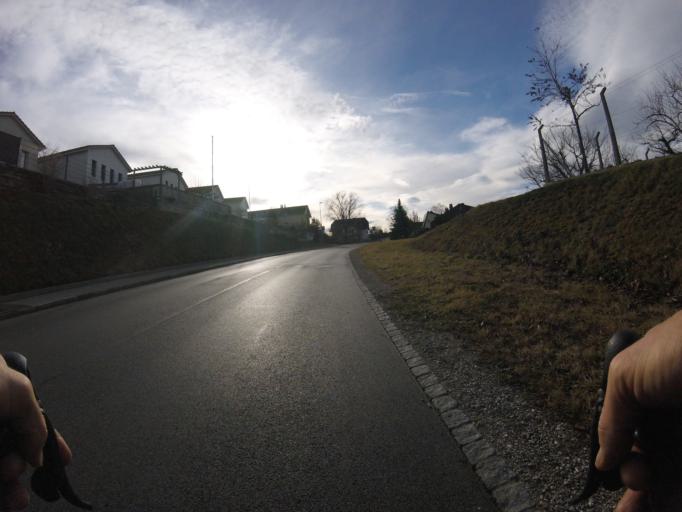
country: CH
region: Fribourg
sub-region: Sense District
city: Ueberstorf
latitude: 46.8618
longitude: 7.3136
